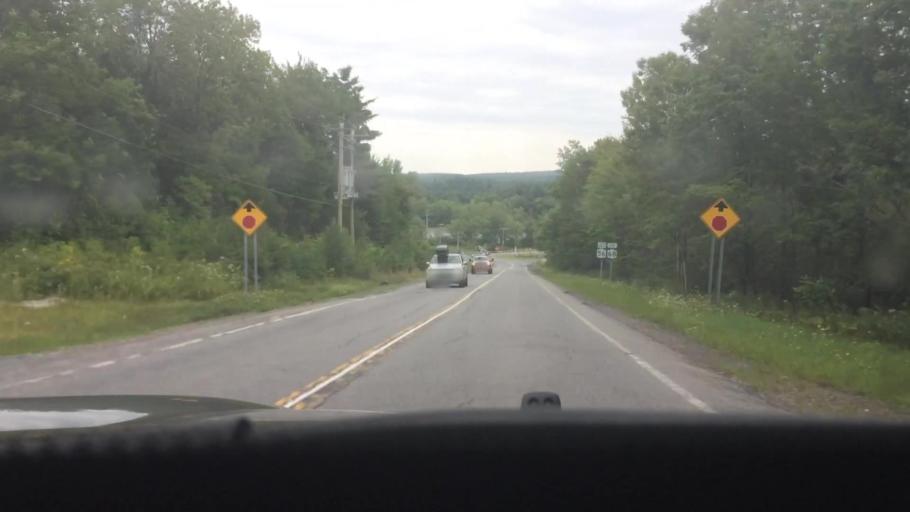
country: US
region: New York
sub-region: St. Lawrence County
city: Hannawa Falls
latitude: 44.5497
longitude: -74.9398
